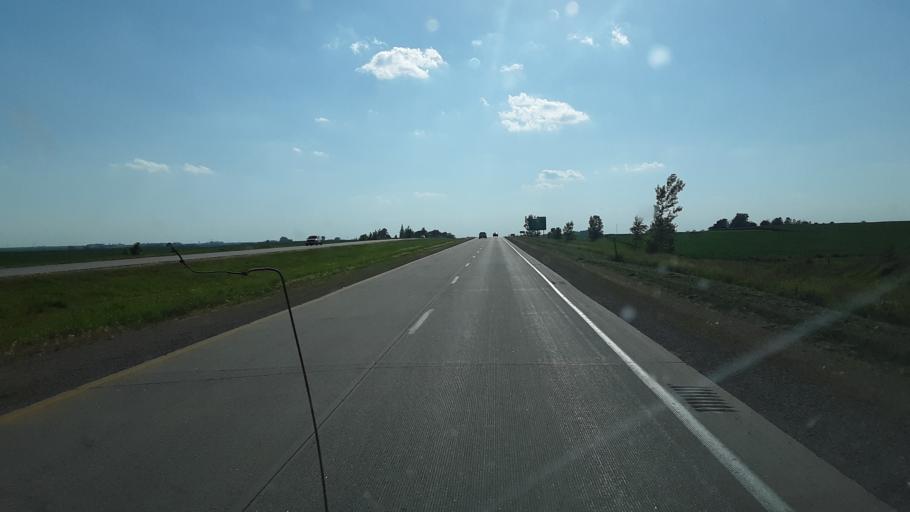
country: US
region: Iowa
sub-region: Grundy County
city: Grundy Center
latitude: 42.4631
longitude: -92.7381
